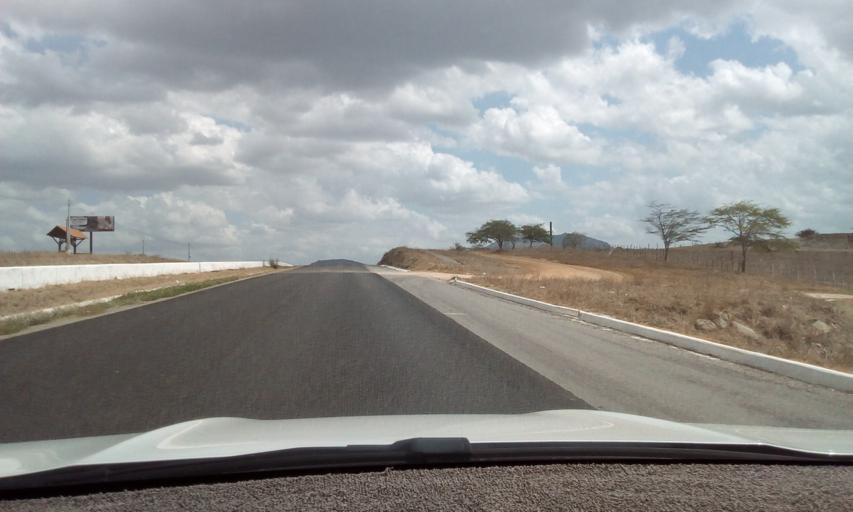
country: BR
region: Pernambuco
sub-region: Toritama
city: Toritama
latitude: -8.0421
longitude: -36.0512
